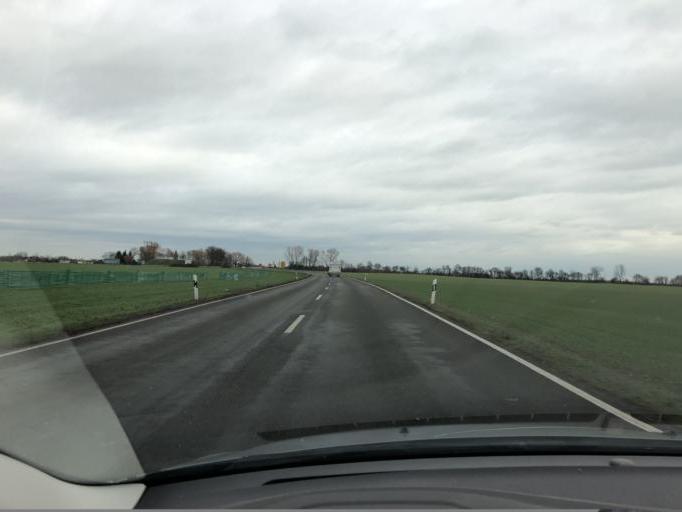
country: DE
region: Saxony
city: Grossposna
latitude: 51.2792
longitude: 12.4403
